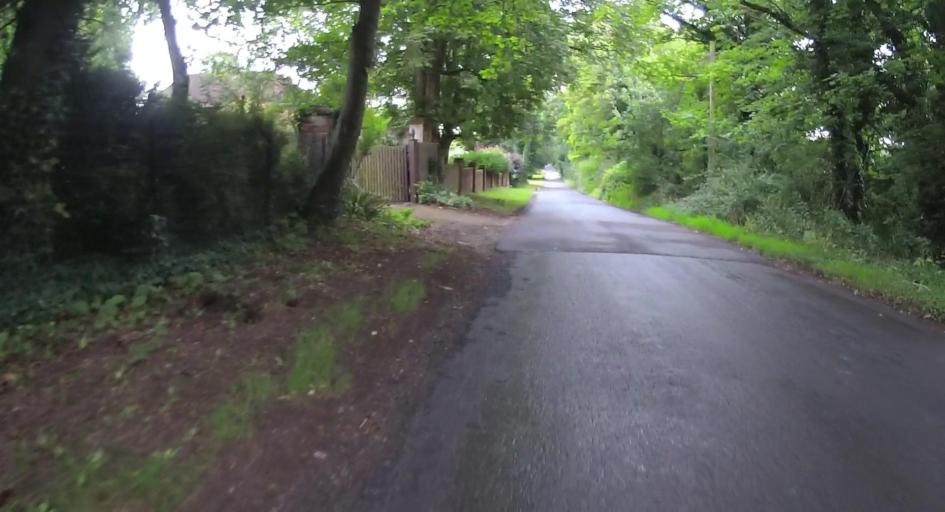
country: GB
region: England
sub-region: Hampshire
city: Andover
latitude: 51.2125
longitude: -1.4354
